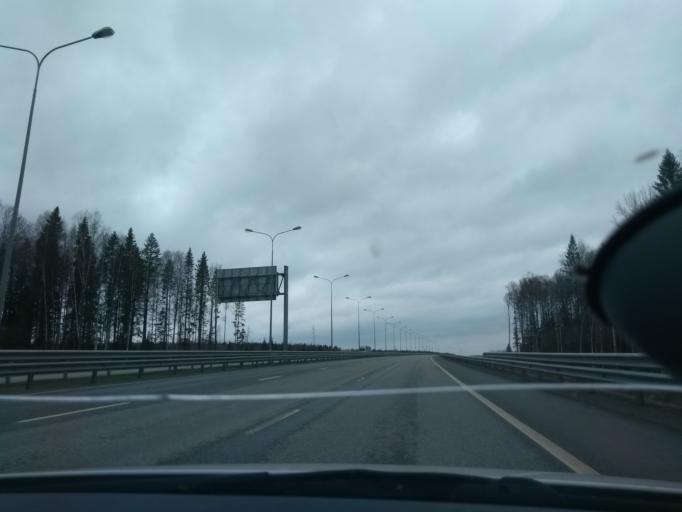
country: RU
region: Perm
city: Bershet'
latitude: 57.7027
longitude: 56.3741
